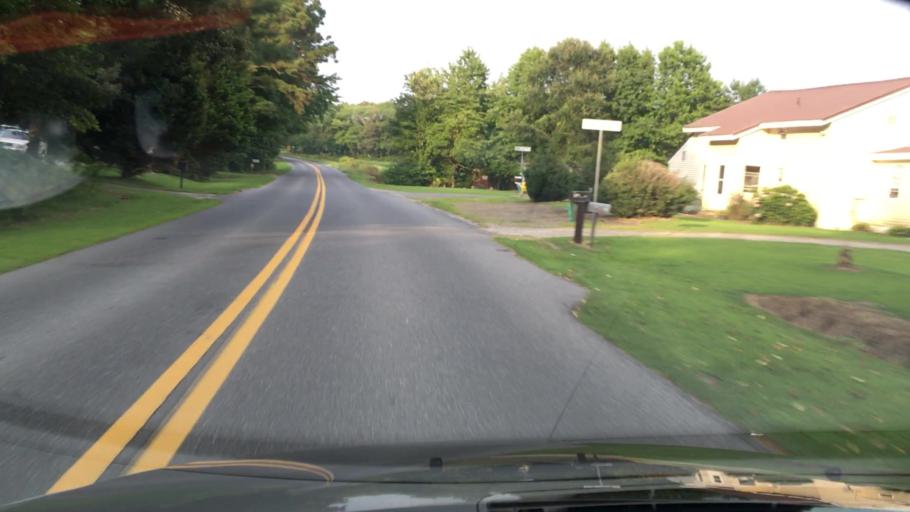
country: US
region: Maryland
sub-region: Worcester County
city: Ocean Pines
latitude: 38.4684
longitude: -75.1443
